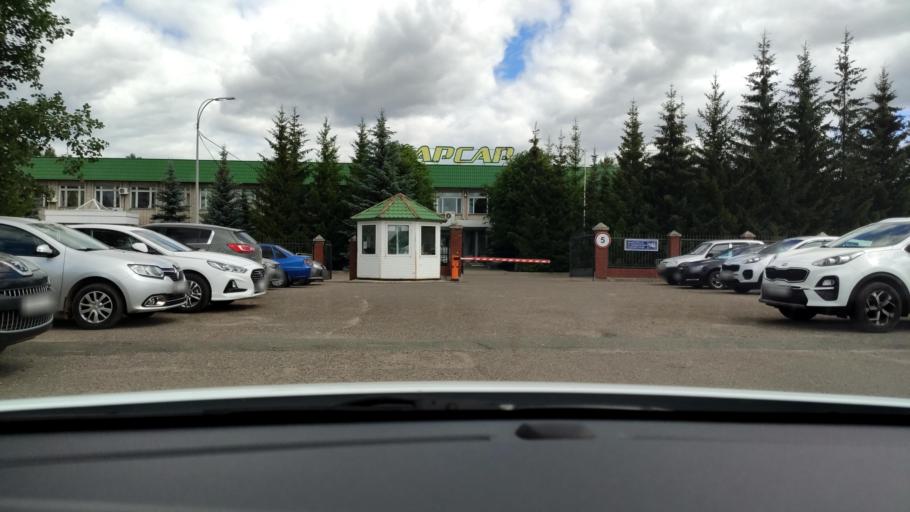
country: RU
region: Tatarstan
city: Stolbishchi
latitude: 55.7289
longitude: 49.1967
